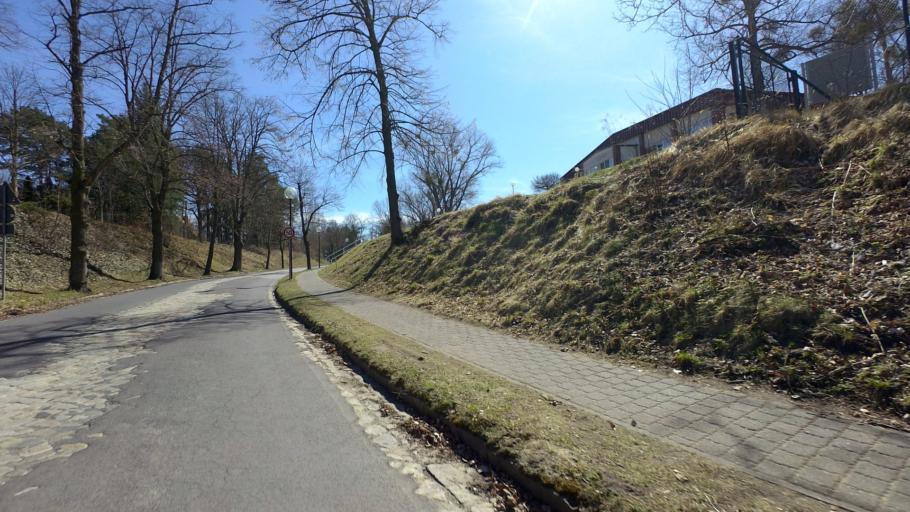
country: DE
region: Brandenburg
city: Teupitz
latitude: 52.1343
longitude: 13.6157
